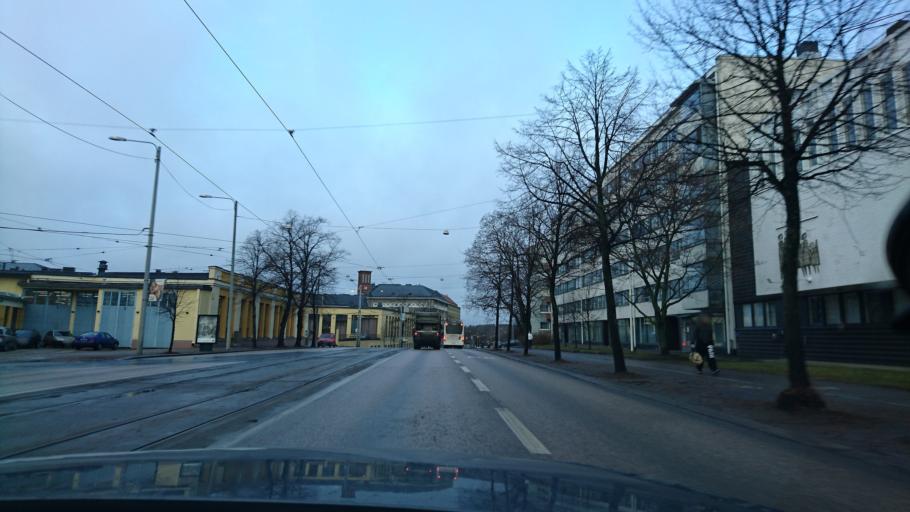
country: FI
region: Uusimaa
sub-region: Helsinki
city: Helsinki
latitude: 60.1943
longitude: 24.9639
